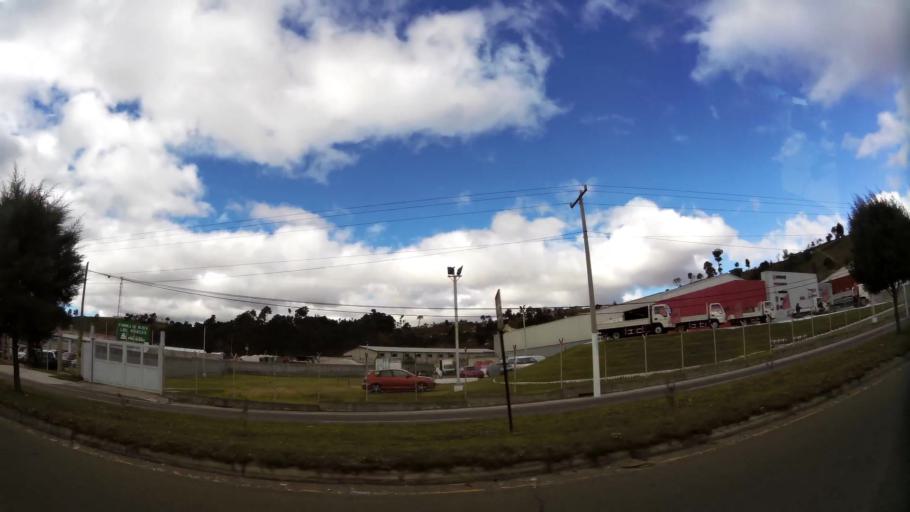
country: GT
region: Quetzaltenango
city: Salcaja
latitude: 14.8689
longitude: -91.4677
